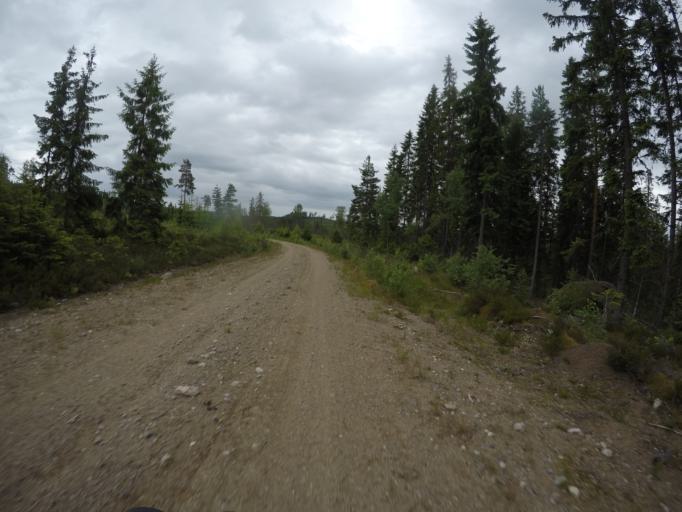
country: SE
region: Dalarna
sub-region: Ludvika Kommun
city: Abborrberget
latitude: 60.0597
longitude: 14.5645
